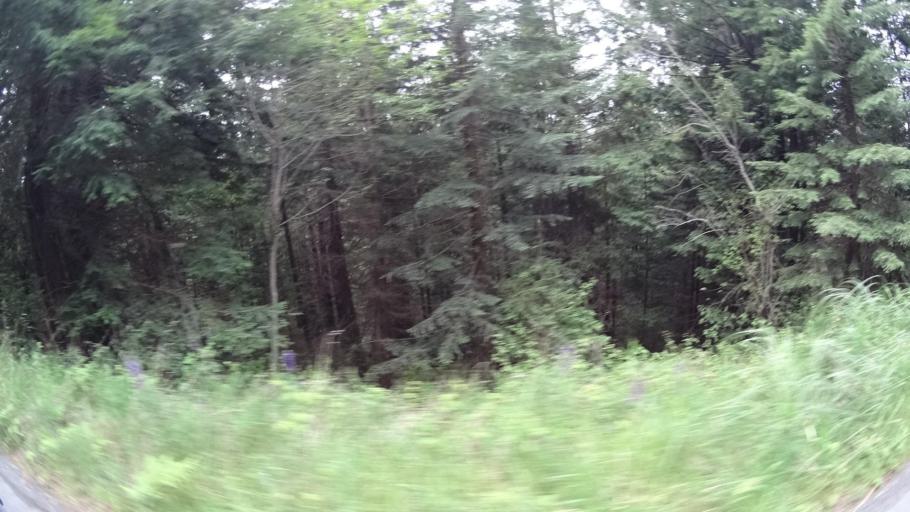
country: US
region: California
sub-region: Humboldt County
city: Blue Lake
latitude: 40.8723
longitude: -123.9712
